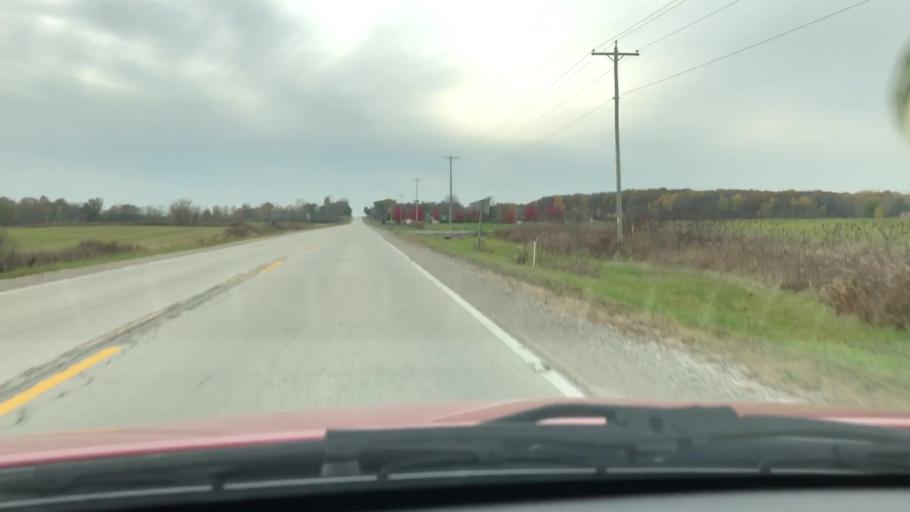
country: US
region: Wisconsin
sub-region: Brown County
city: Oneida
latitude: 44.4443
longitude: -88.2529
